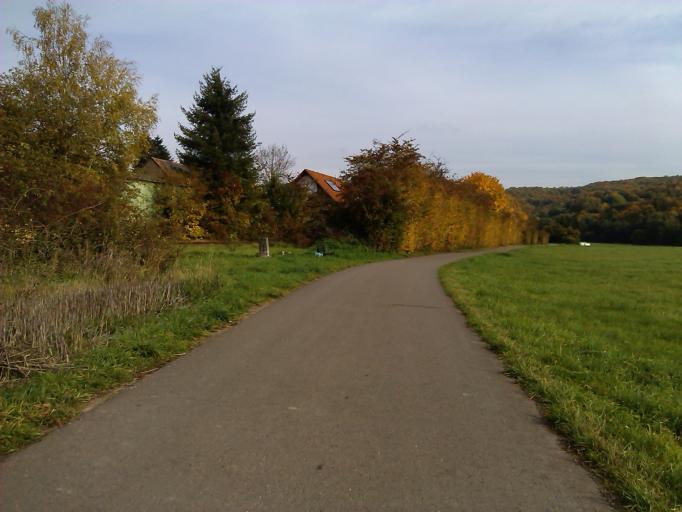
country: DE
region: Rheinland-Pfalz
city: Medard
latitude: 49.6652
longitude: 7.6077
